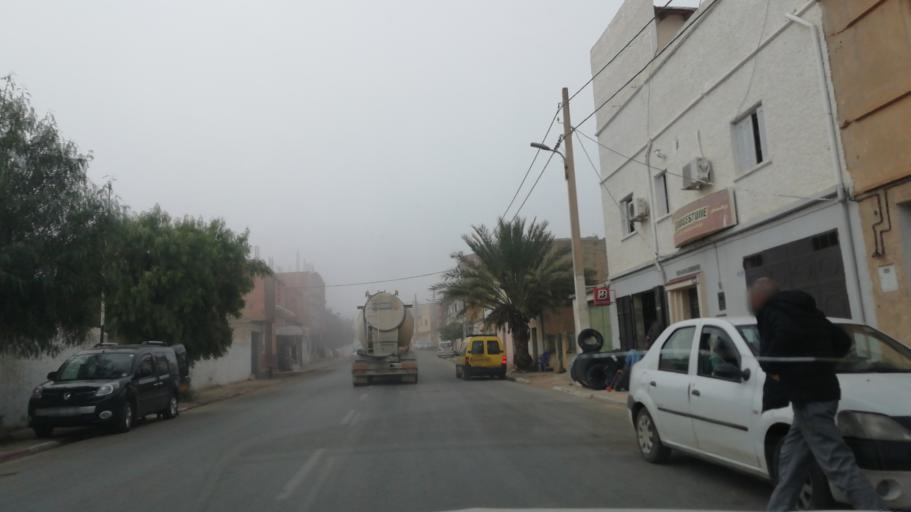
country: DZ
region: Mascara
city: Mascara
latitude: 35.5197
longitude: 0.3105
